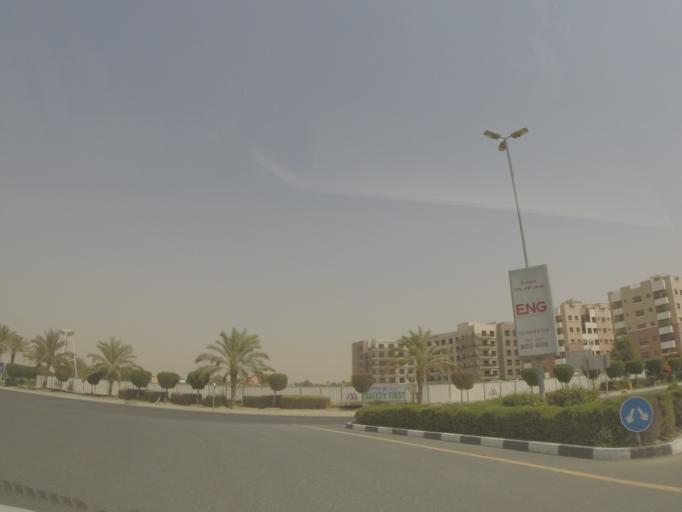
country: AE
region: Dubai
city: Dubai
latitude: 25.0022
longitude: 55.1547
